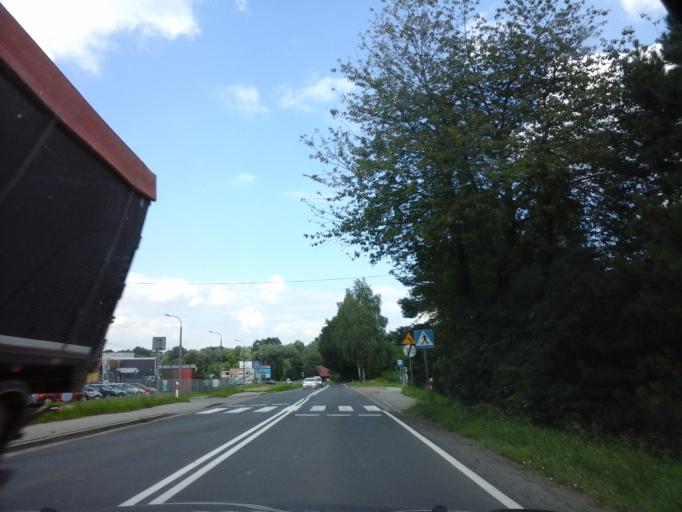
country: PL
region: Lesser Poland Voivodeship
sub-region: Powiat suski
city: Sucha Beskidzka
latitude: 49.7565
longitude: 19.6037
